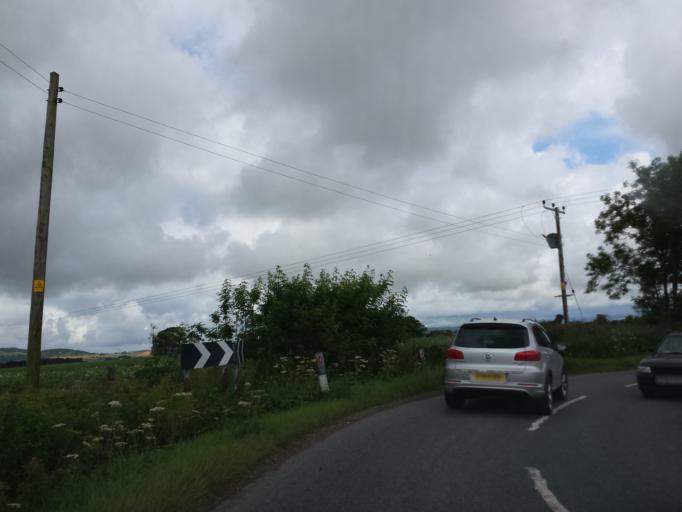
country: GB
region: Scotland
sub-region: Fife
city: Strathkinness
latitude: 56.3501
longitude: -2.8718
